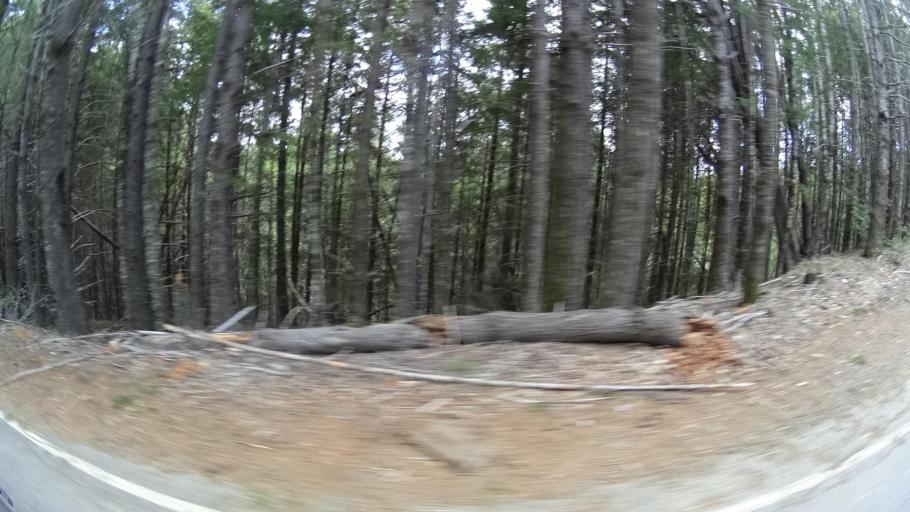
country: US
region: California
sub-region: Humboldt County
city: Redway
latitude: 40.0545
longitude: -123.9950
